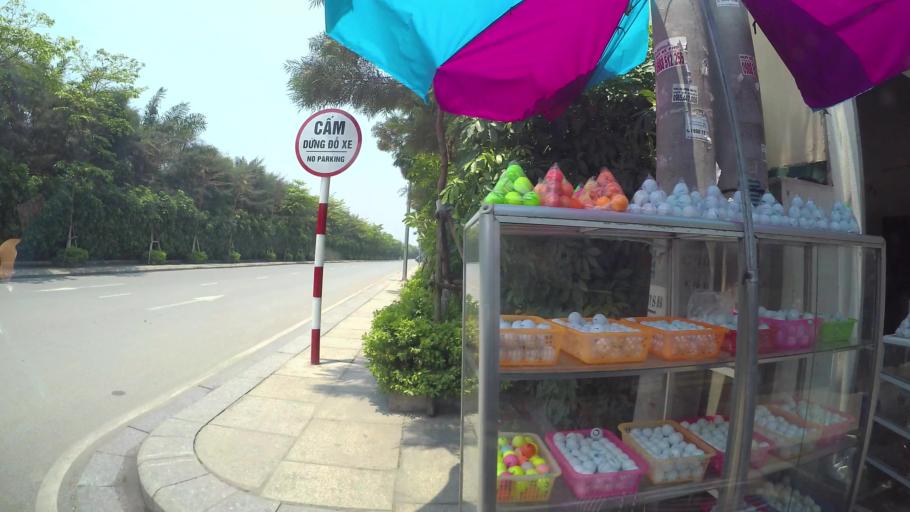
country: VN
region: Ha Noi
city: Trau Quy
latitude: 21.0330
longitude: 105.8984
